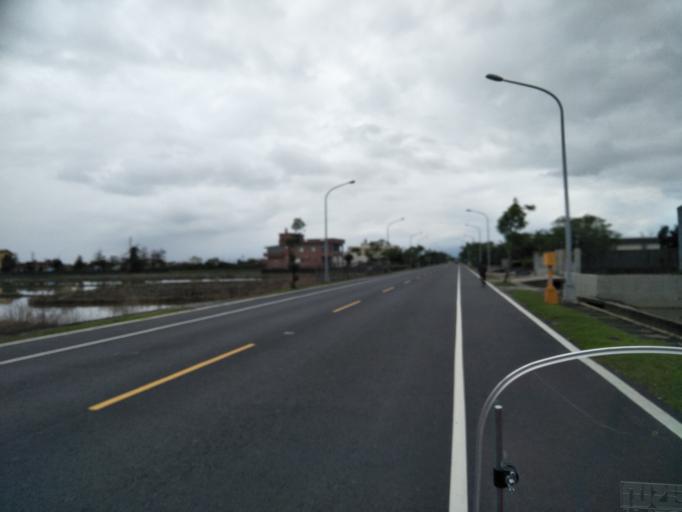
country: TW
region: Taiwan
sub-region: Yilan
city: Yilan
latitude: 24.8025
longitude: 121.7886
